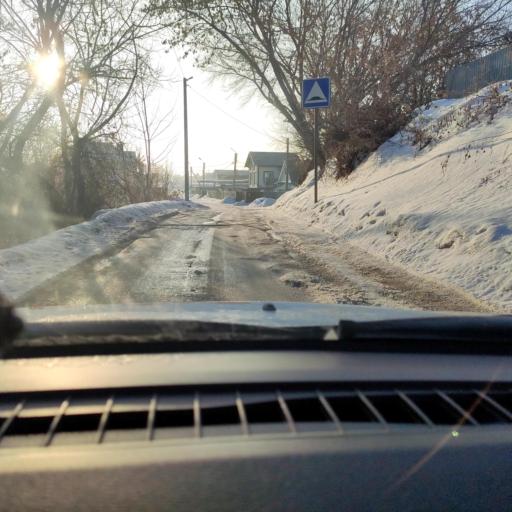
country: RU
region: Samara
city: Novokuybyshevsk
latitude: 53.1193
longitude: 49.9485
